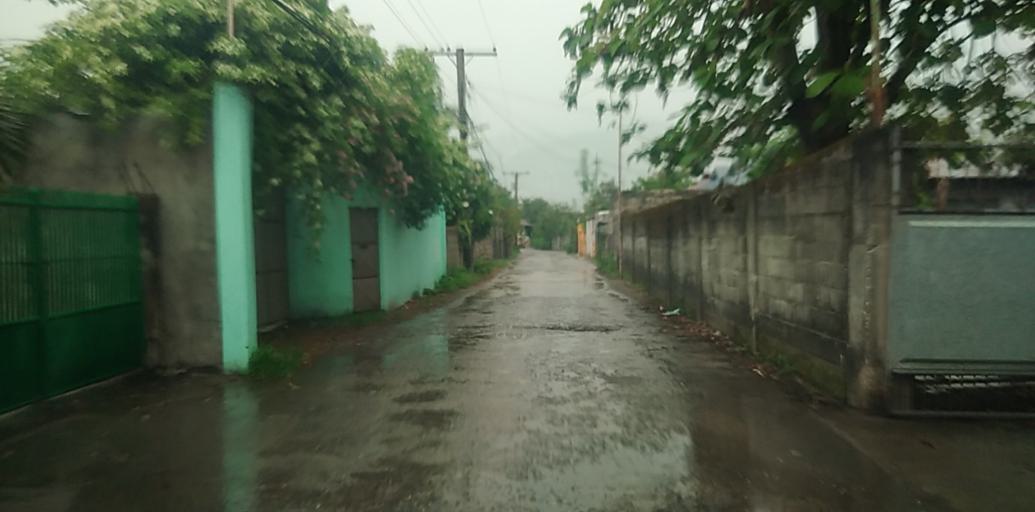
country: PH
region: Central Luzon
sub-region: Province of Pampanga
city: Arenas
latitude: 15.1771
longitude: 120.6797
